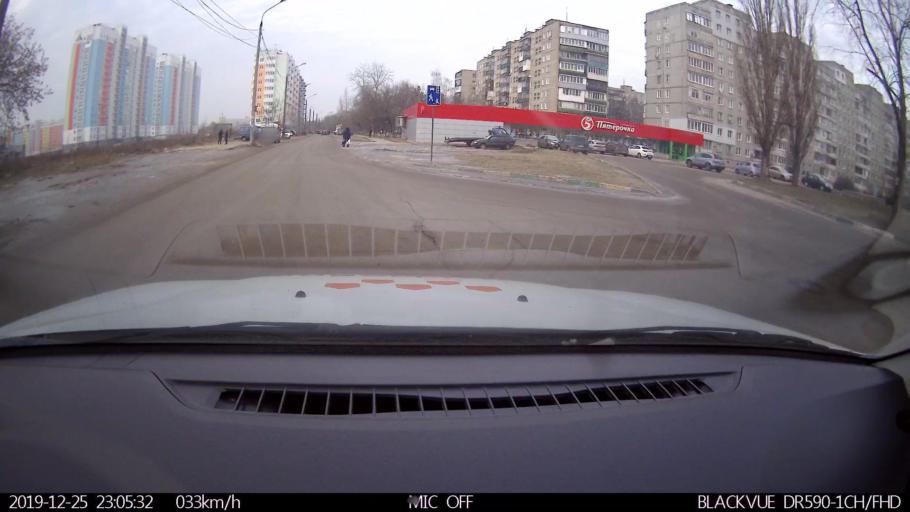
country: RU
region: Nizjnij Novgorod
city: Gorbatovka
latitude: 56.3603
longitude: 43.8062
